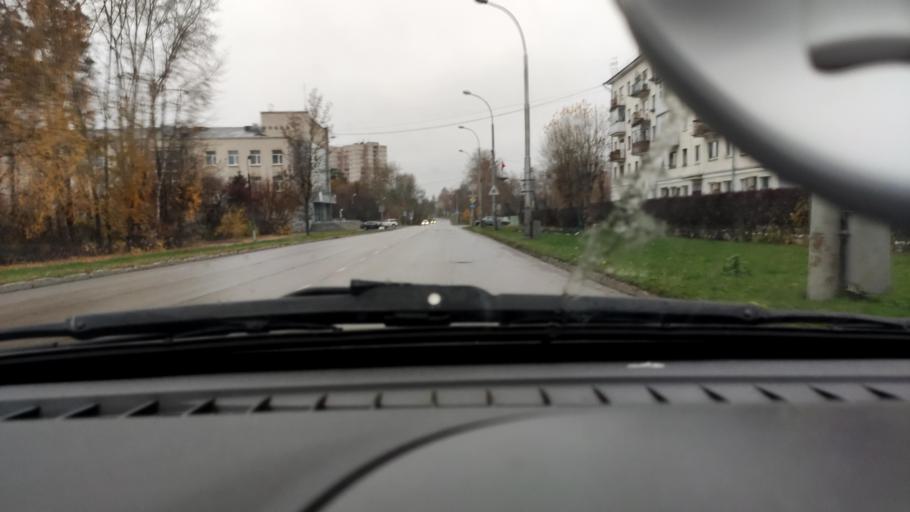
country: RU
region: Perm
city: Kultayevo
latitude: 57.9990
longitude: 55.9538
